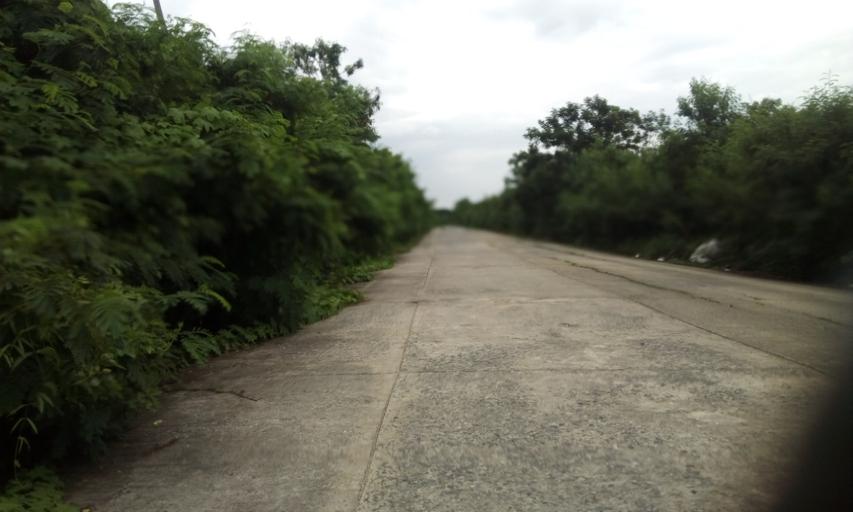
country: TH
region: Pathum Thani
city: Nong Suea
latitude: 14.0678
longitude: 100.8352
